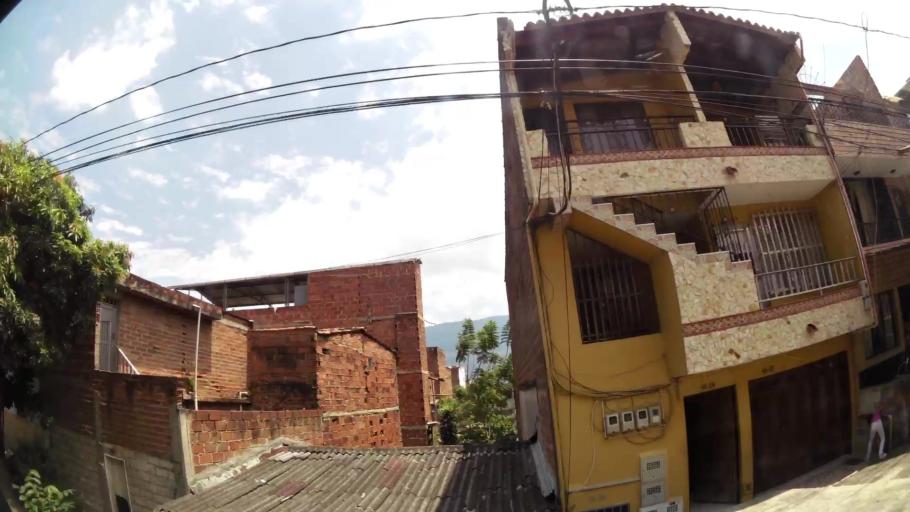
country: CO
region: Antioquia
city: Bello
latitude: 6.2963
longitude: -75.5761
